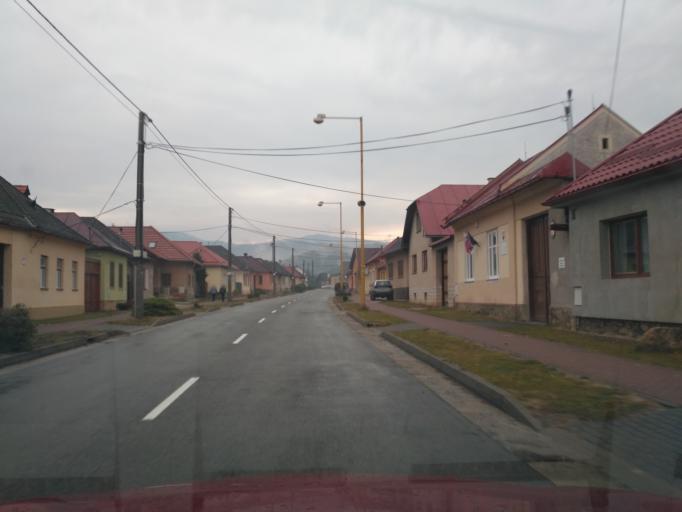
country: SK
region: Kosicky
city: Medzev
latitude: 48.7024
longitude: 20.8873
